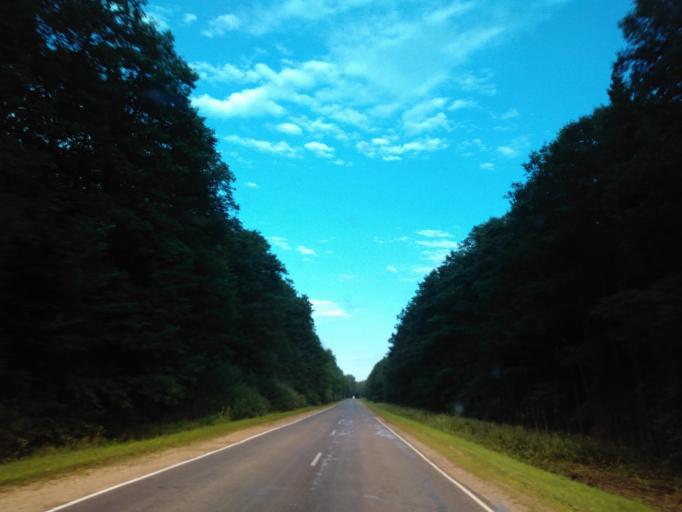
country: BY
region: Minsk
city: Uzda
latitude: 53.4239
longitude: 27.3845
